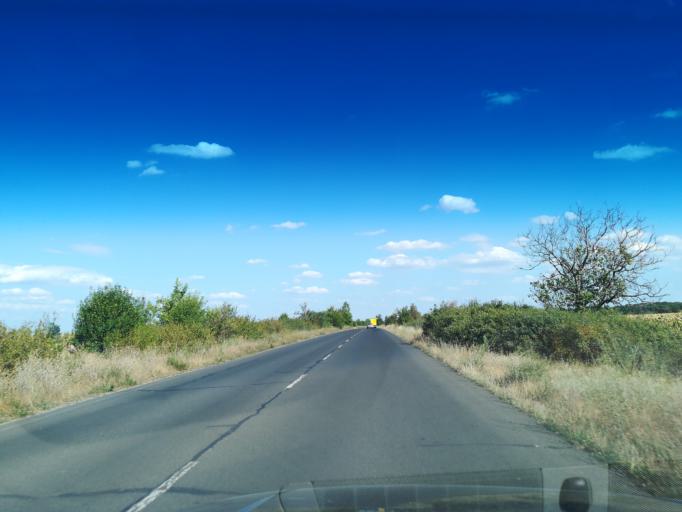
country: BG
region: Stara Zagora
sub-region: Obshtina Chirpan
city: Chirpan
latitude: 42.0645
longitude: 25.2314
